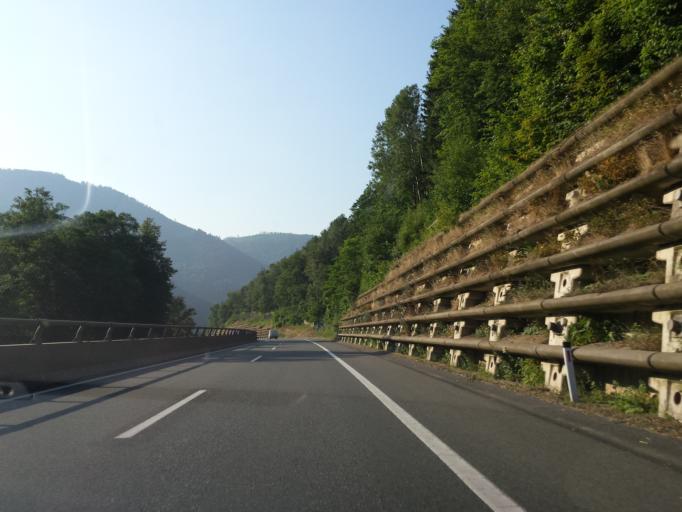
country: AT
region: Styria
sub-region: Politischer Bezirk Graz-Umgebung
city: Rothelstein
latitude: 47.3190
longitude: 15.3674
